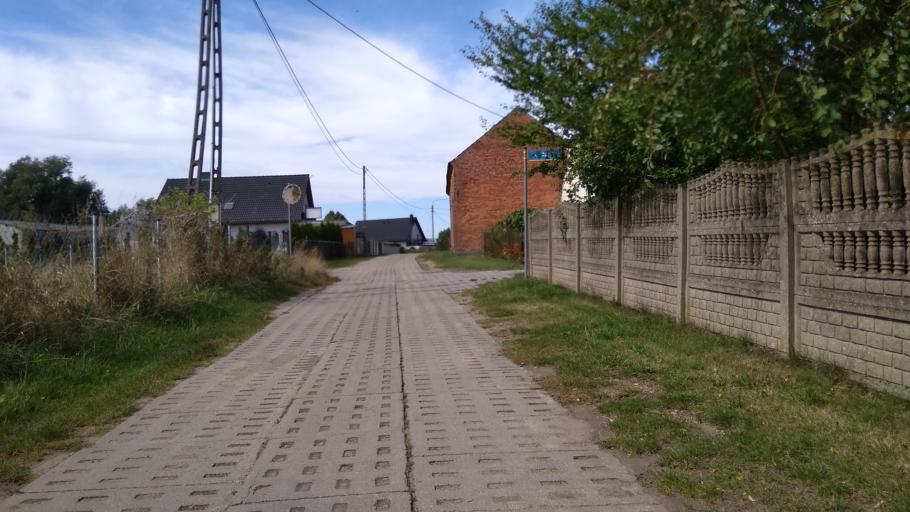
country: PL
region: West Pomeranian Voivodeship
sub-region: Powiat slawienski
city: Darlowo
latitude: 54.5105
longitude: 16.5149
